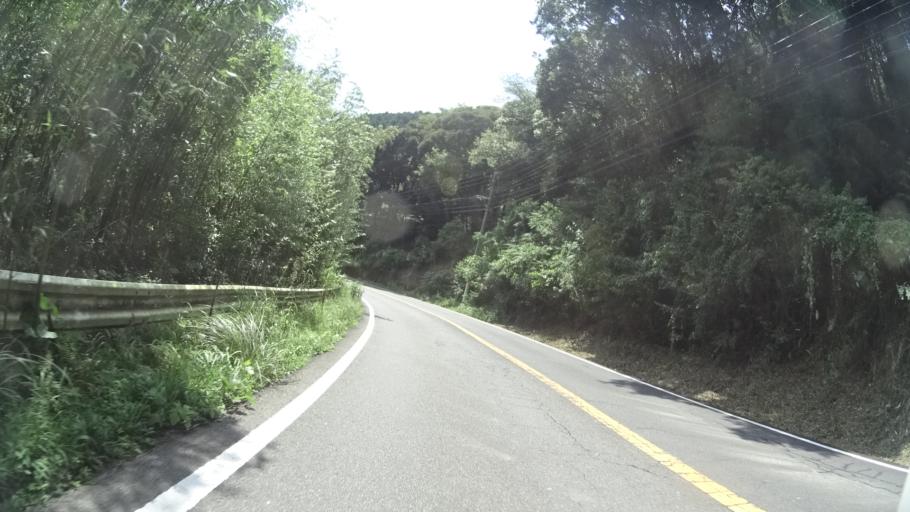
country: JP
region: Kagoshima
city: Kokubu-matsuki
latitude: 31.8699
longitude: 130.7889
